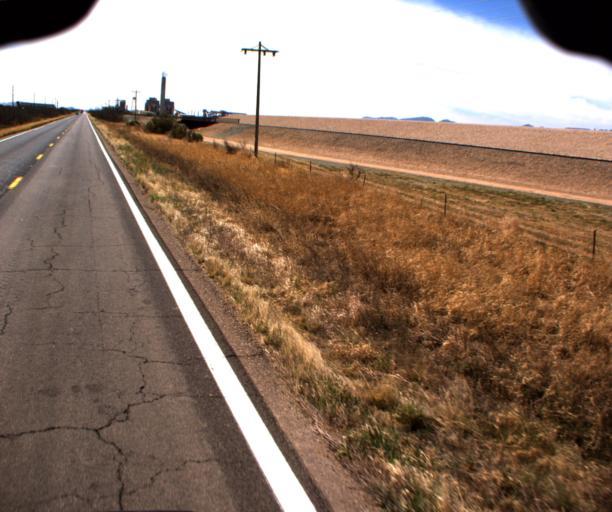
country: US
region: Arizona
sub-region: Cochise County
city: Willcox
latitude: 32.0789
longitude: -109.9006
